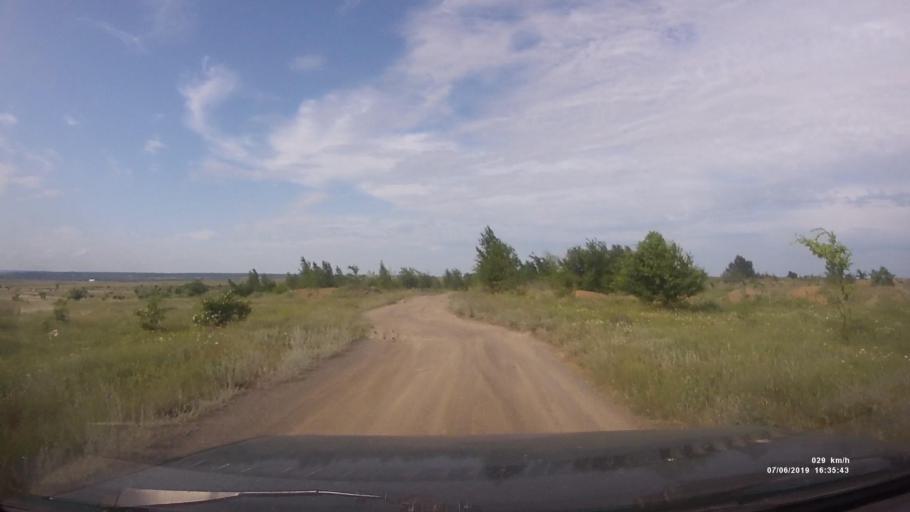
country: RU
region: Rostov
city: Staraya Stanitsa
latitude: 48.2522
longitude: 40.3490
